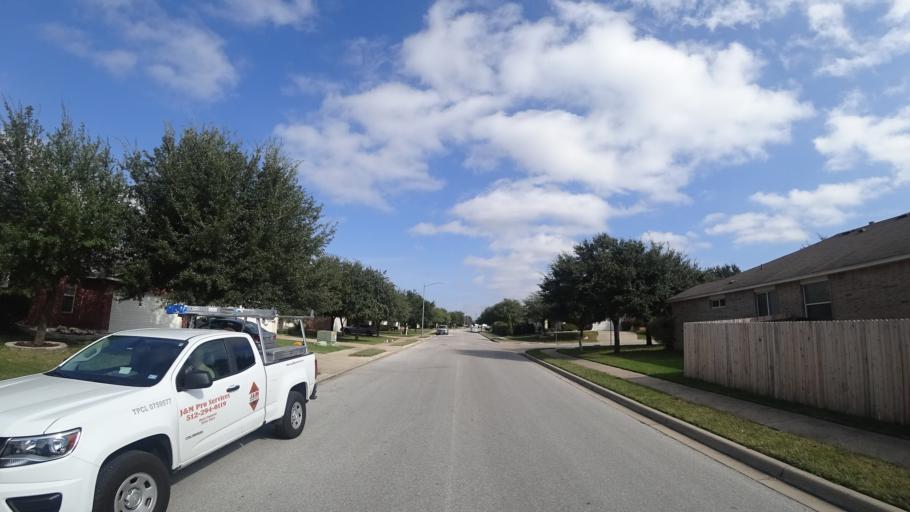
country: US
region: Texas
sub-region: Travis County
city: Pflugerville
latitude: 30.4265
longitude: -97.6428
